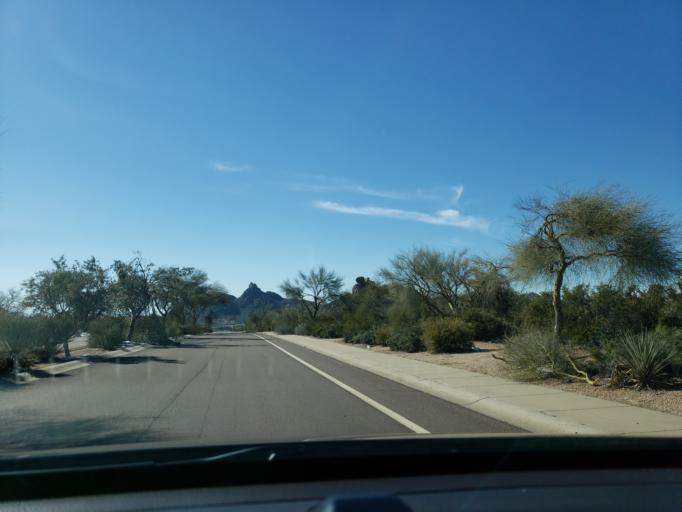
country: US
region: Arizona
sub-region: Maricopa County
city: Carefree
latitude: 33.7269
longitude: -111.8348
